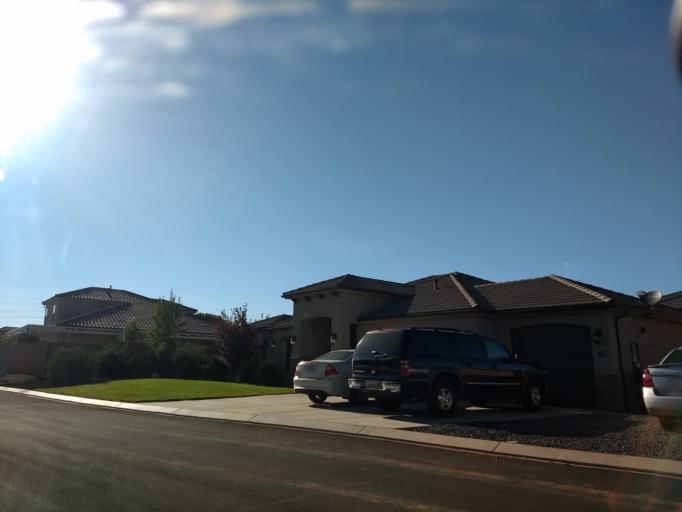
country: US
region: Utah
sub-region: Washington County
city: Washington
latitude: 37.1214
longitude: -113.5067
